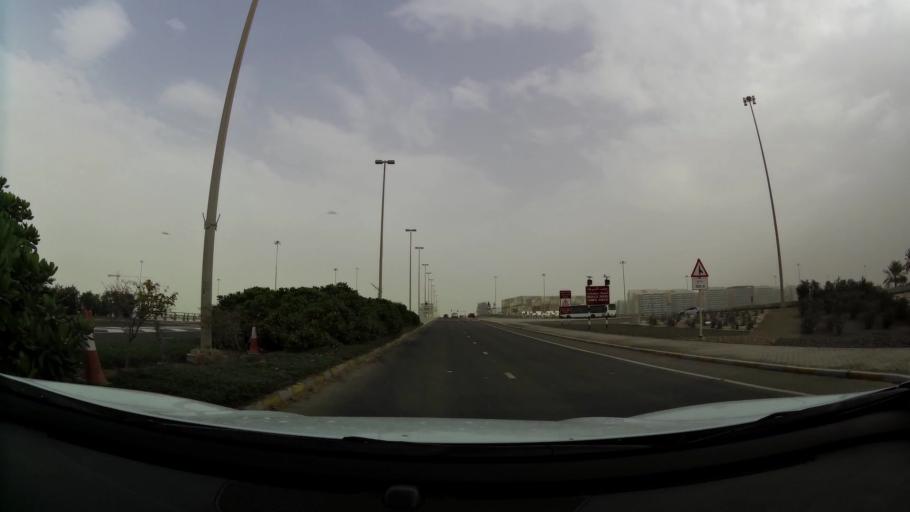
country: AE
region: Abu Dhabi
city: Abu Dhabi
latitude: 24.4437
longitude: 54.6011
